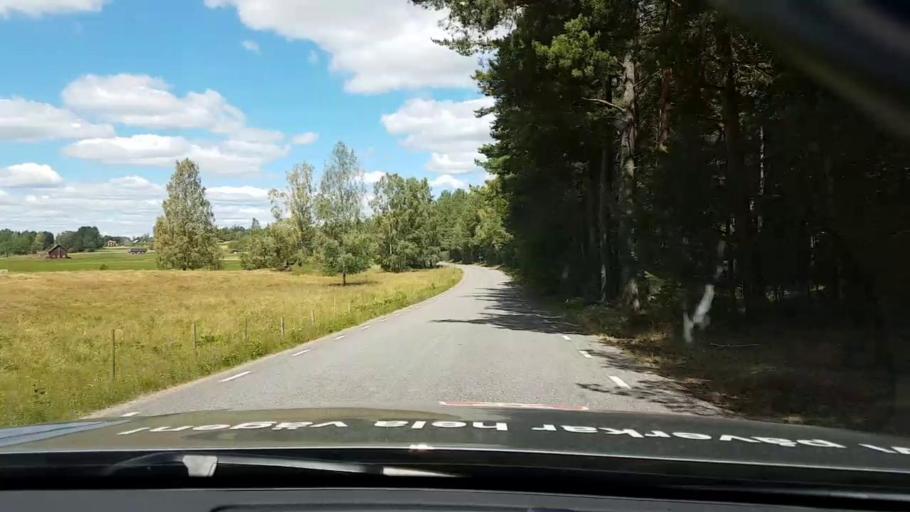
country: SE
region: Kalmar
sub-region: Vasterviks Kommun
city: Forserum
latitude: 58.0204
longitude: 16.5744
